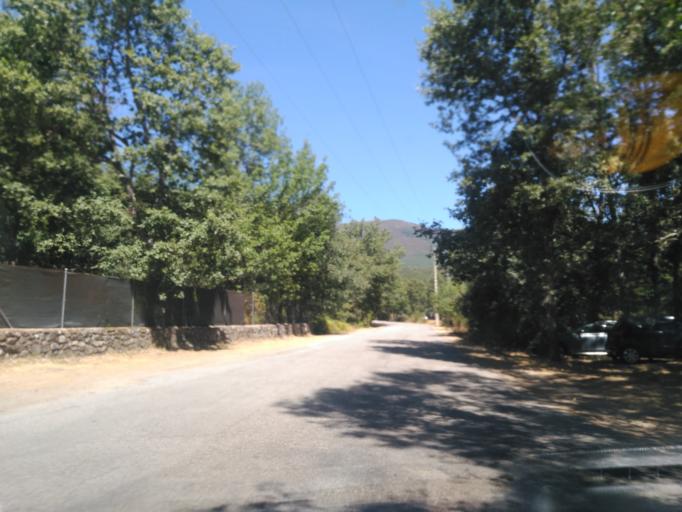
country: ES
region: Castille and Leon
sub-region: Provincia de Zamora
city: Galende
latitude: 42.1220
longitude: -6.6981
